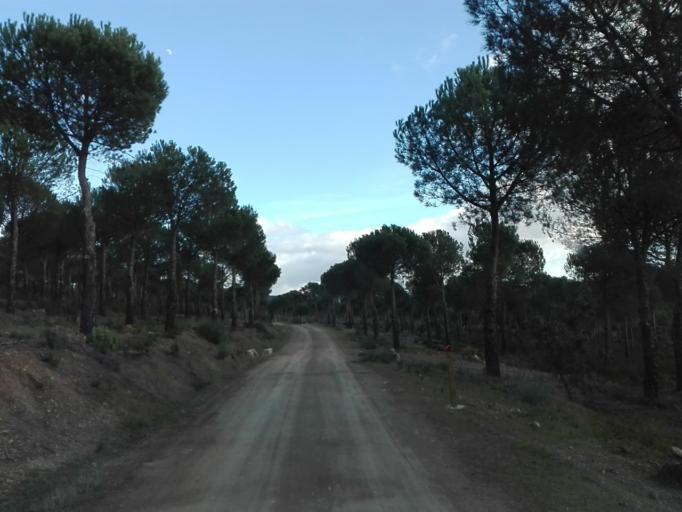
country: ES
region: Extremadura
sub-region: Provincia de Badajoz
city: Reina
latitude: 38.1770
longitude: -5.9713
